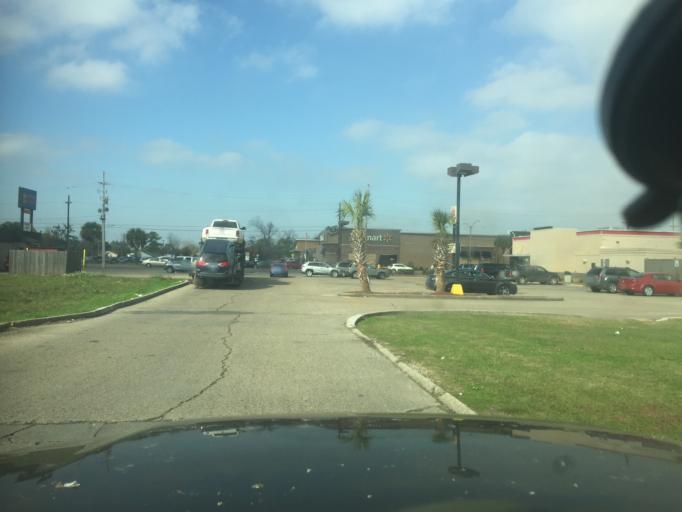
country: US
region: Louisiana
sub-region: Saint Bernard Parish
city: Arabi
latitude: 30.0038
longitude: -90.0377
